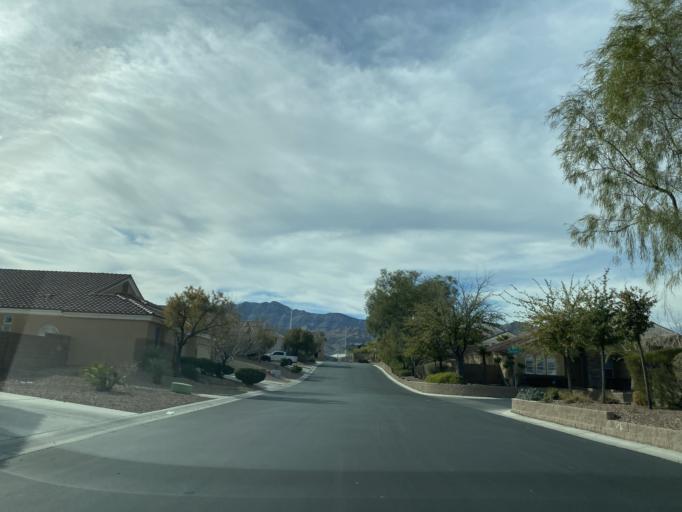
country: US
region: Nevada
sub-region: Clark County
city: Summerlin South
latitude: 36.2736
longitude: -115.3245
